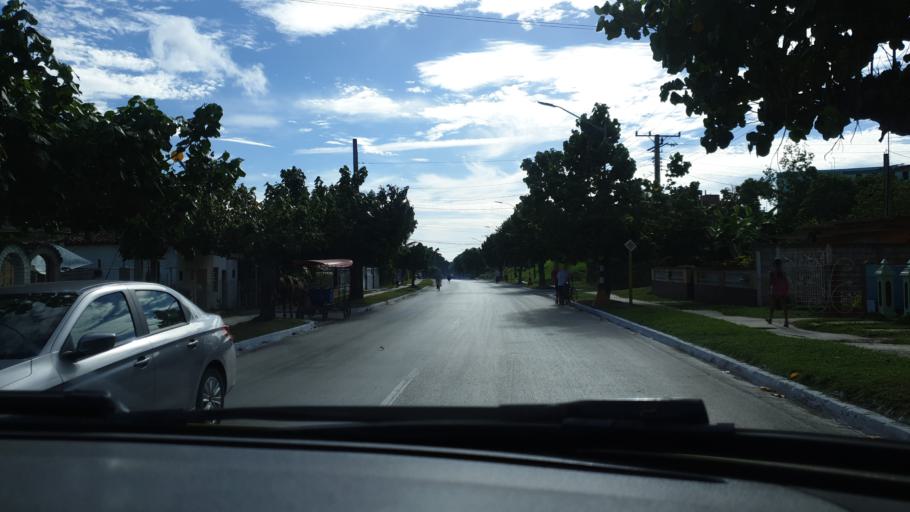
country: CU
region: Villa Clara
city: Santa Clara
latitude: 22.4135
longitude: -79.9515
